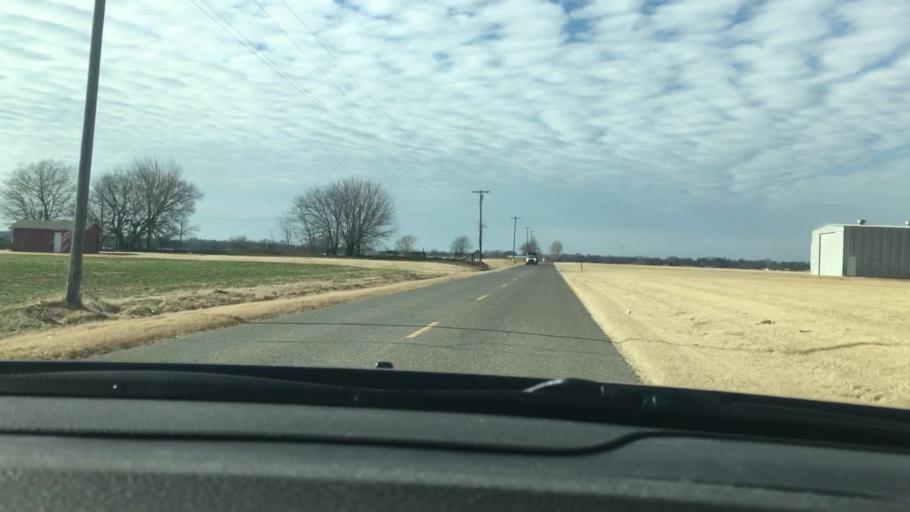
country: US
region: Oklahoma
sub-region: Garvin County
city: Pauls Valley
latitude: 34.7387
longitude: -97.1853
